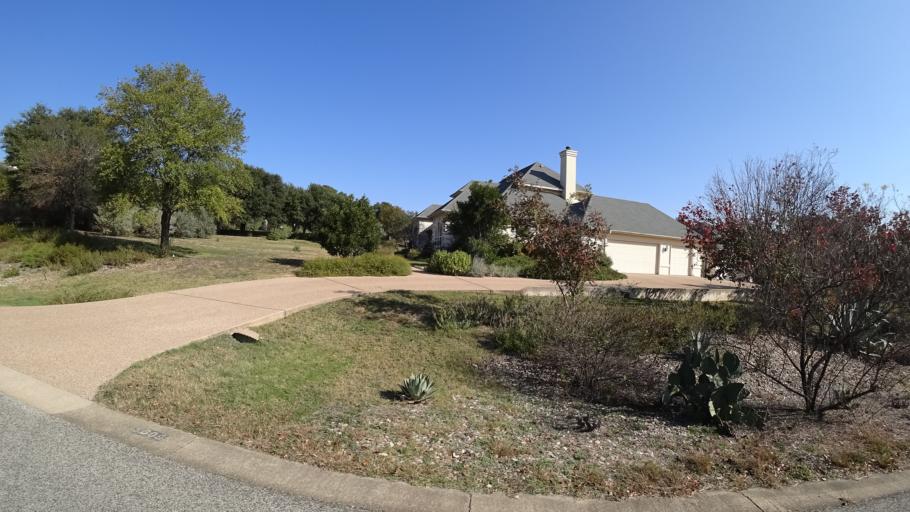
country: US
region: Texas
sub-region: Travis County
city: West Lake Hills
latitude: 30.3694
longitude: -97.8239
